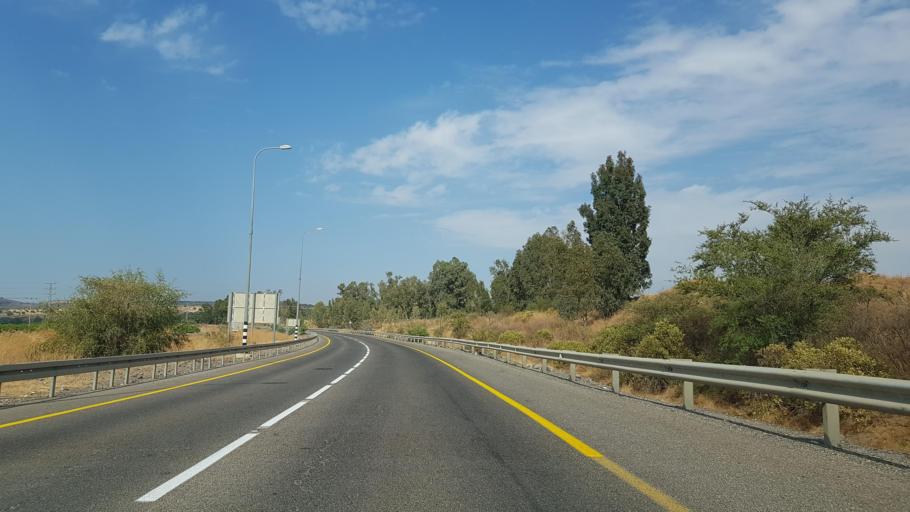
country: SY
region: Quneitra
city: Al Butayhah
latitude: 32.8837
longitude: 35.6607
